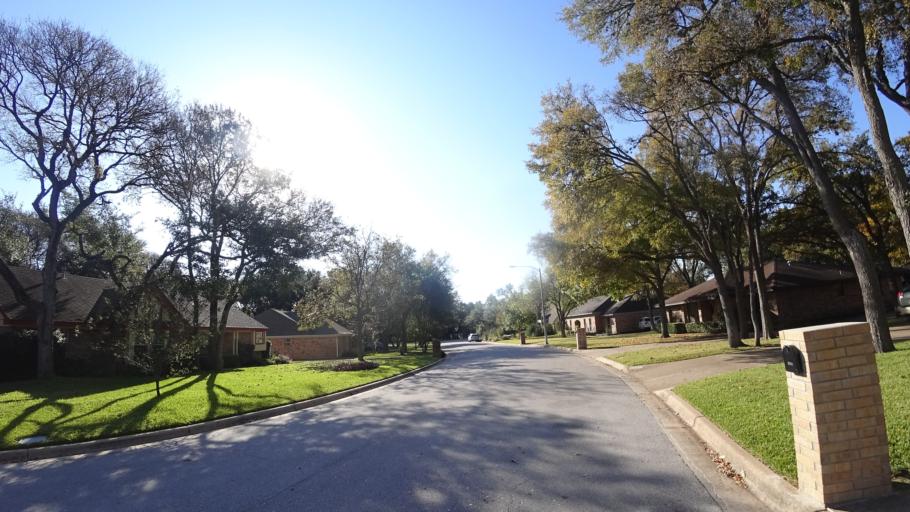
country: US
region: Texas
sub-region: Travis County
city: Shady Hollow
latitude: 30.2220
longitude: -97.8475
